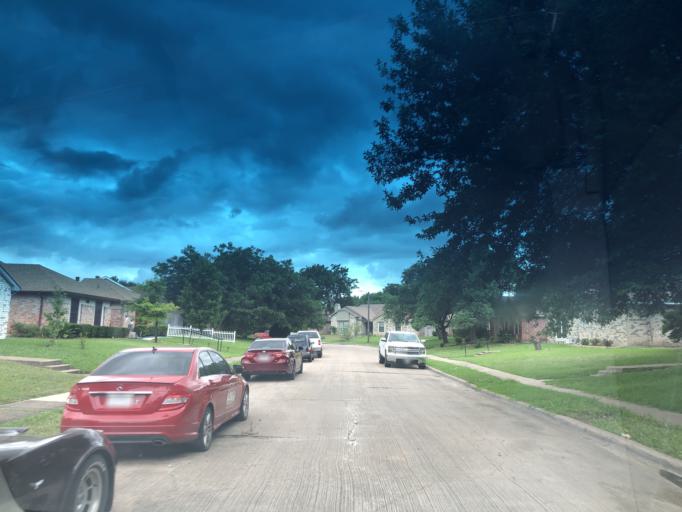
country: US
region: Texas
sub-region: Dallas County
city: Grand Prairie
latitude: 32.7004
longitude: -97.0049
